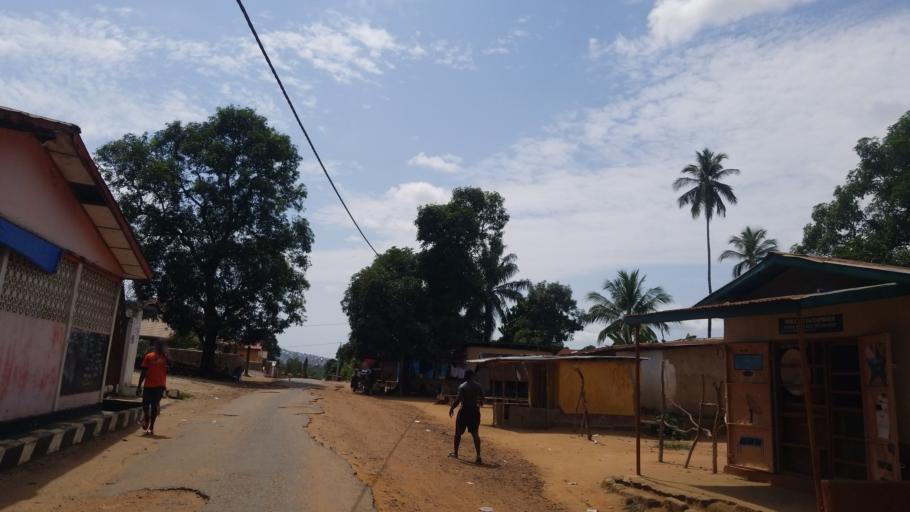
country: SL
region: Western Area
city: Waterloo
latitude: 8.3137
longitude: -13.0558
